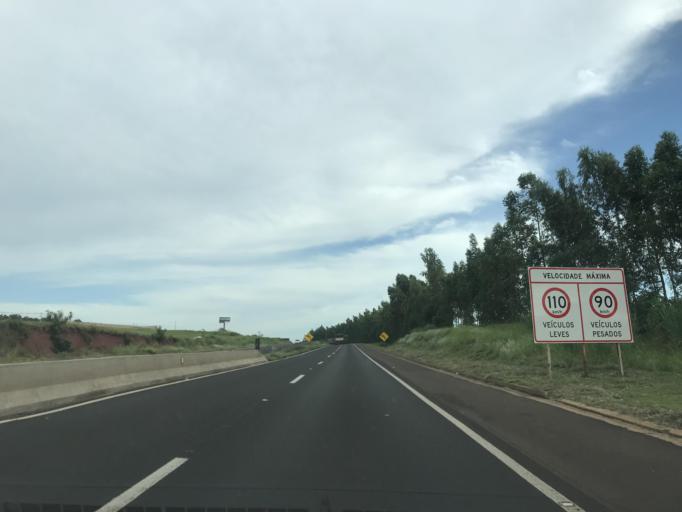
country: BR
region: Parana
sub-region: Alto Parana
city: Alto Parana
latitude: -23.1246
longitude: -52.3075
